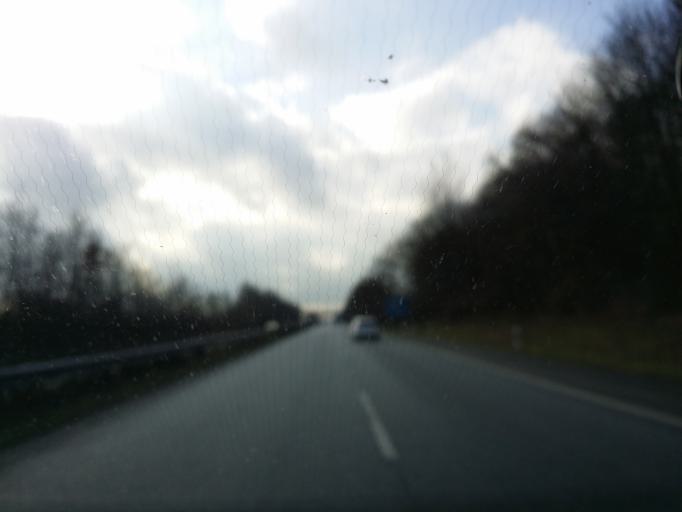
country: DE
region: Schleswig-Holstein
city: Hassmoor
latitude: 54.3133
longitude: 9.7945
